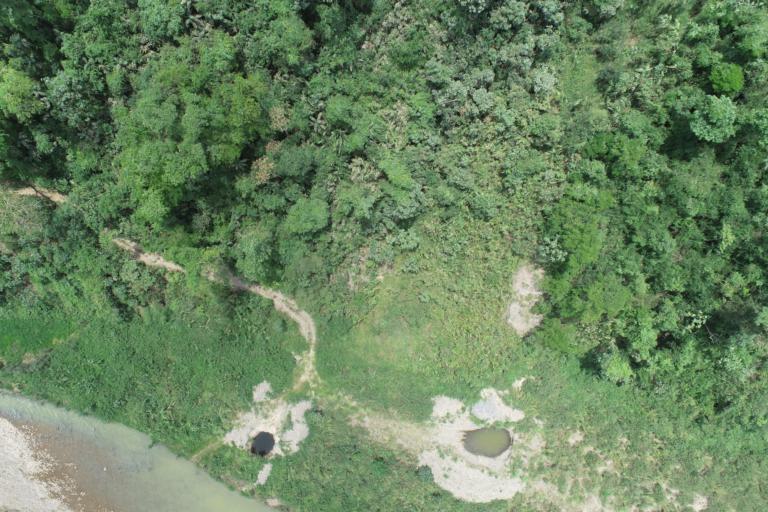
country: BO
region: La Paz
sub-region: Provincia Larecaja
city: Guanay
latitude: -15.7673
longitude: -67.6639
